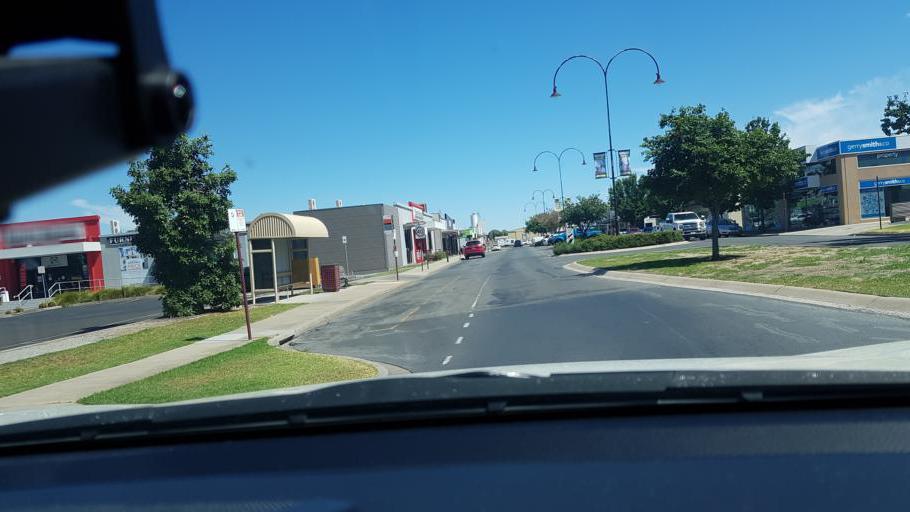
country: AU
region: Victoria
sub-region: Horsham
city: Horsham
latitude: -36.7179
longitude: 142.1996
